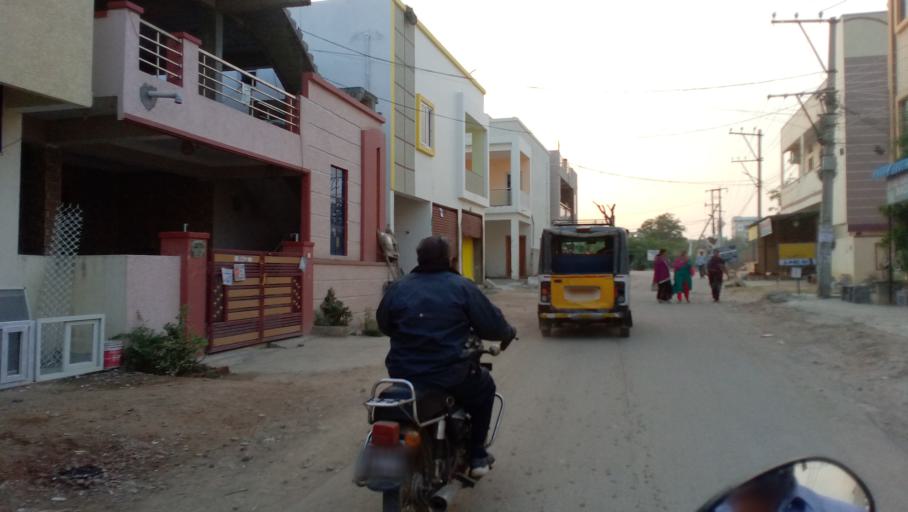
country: IN
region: Telangana
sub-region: Medak
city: Serilingampalle
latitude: 17.5187
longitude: 78.3141
